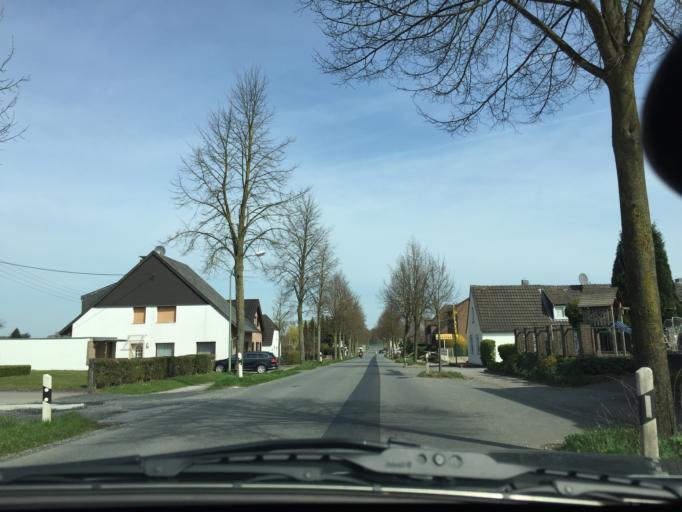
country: DE
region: North Rhine-Westphalia
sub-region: Regierungsbezirk Dusseldorf
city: Goch
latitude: 51.7045
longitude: 6.1563
